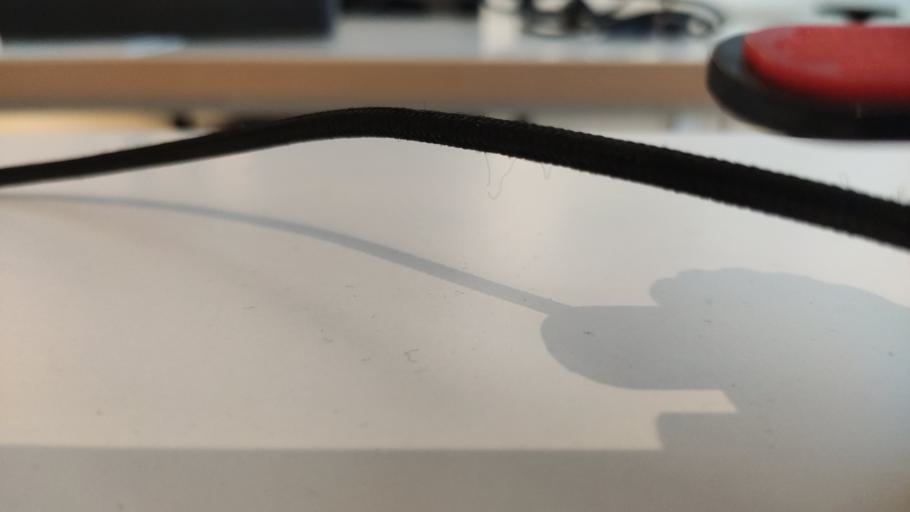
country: RU
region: Moskovskaya
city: Novopetrovskoye
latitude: 55.9455
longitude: 36.4367
